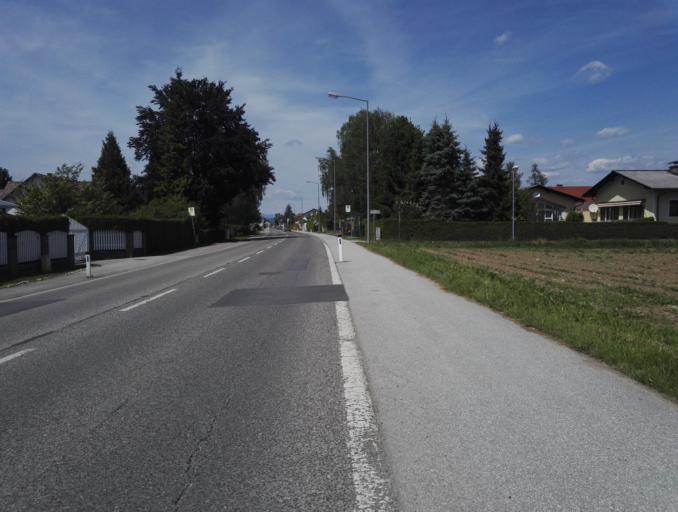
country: AT
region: Styria
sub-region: Politischer Bezirk Graz-Umgebung
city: Gossendorf
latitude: 46.9892
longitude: 15.4572
